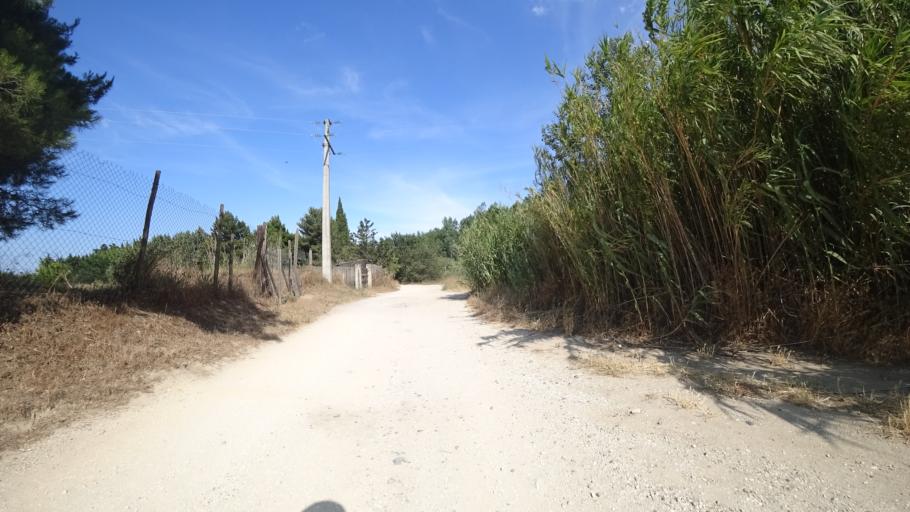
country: FR
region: Languedoc-Roussillon
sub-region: Departement des Pyrenees-Orientales
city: Rivesaltes
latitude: 42.7751
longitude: 2.8636
